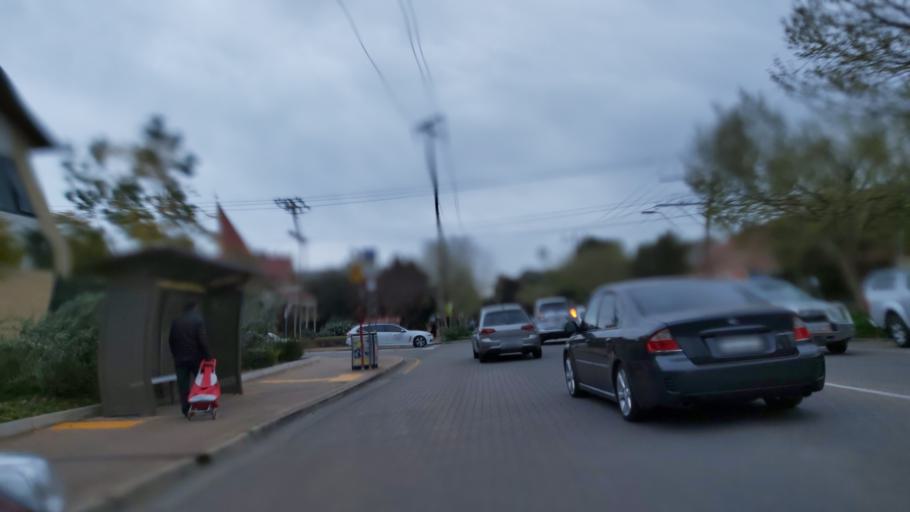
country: AU
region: South Australia
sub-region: Unley
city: Unley
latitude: -34.9453
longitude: 138.5993
